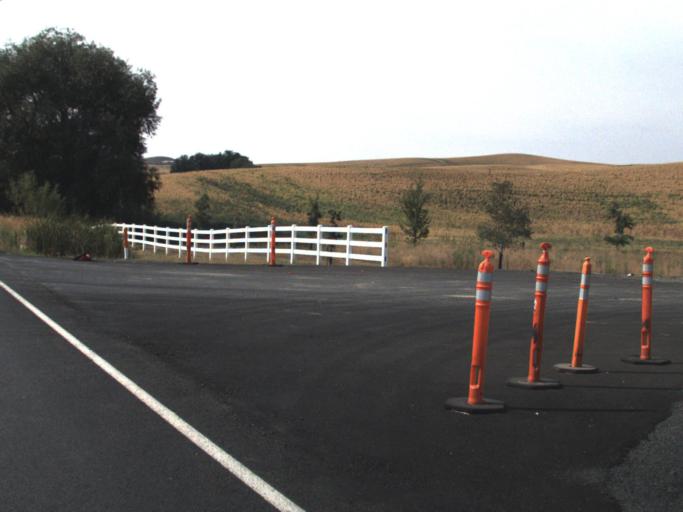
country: US
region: Washington
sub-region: Whitman County
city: Pullman
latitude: 46.7673
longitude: -117.1663
